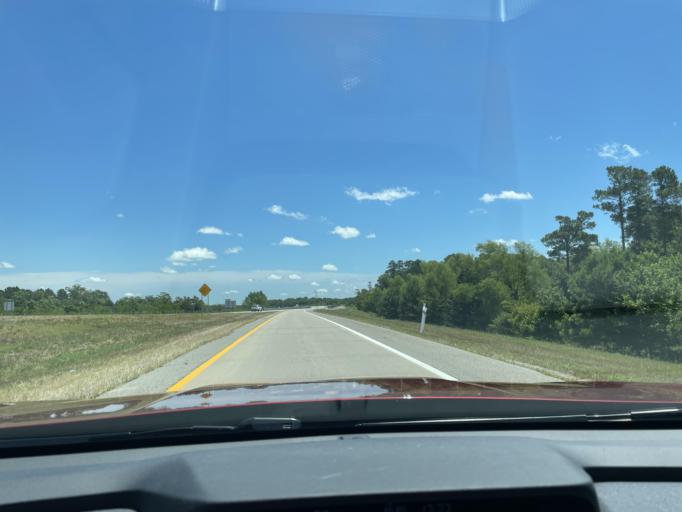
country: US
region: Arkansas
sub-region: Jefferson County
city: Pine Bluff
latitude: 34.1706
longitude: -92.0048
